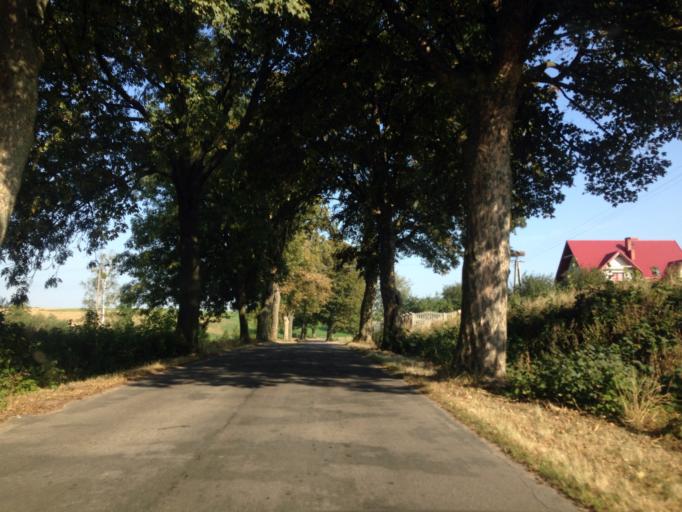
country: PL
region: Kujawsko-Pomorskie
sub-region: Powiat brodnicki
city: Brzozie
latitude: 53.3121
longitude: 19.6069
